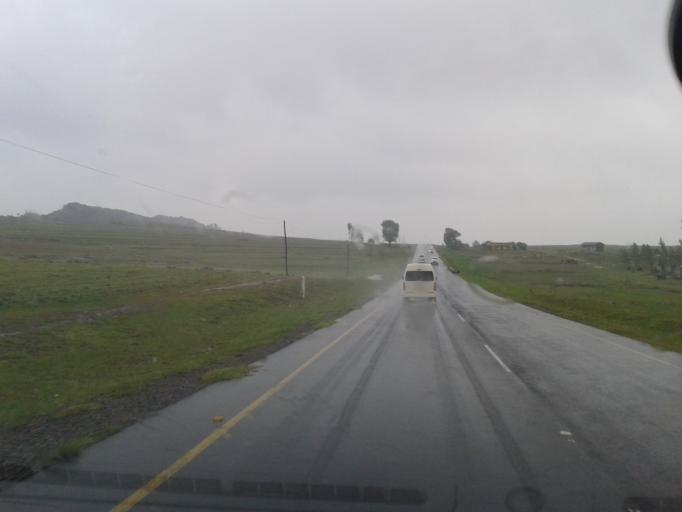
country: LS
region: Mafeteng
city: Mafeteng
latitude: -29.6744
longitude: 27.4487
